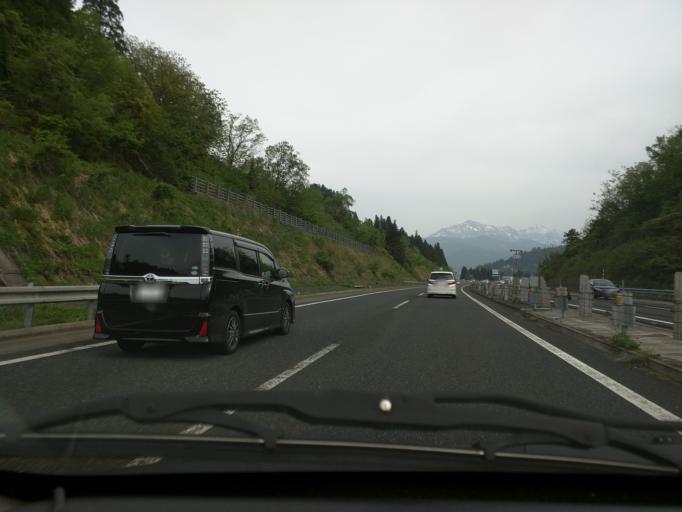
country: JP
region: Niigata
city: Ojiya
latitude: 37.2517
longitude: 138.9333
